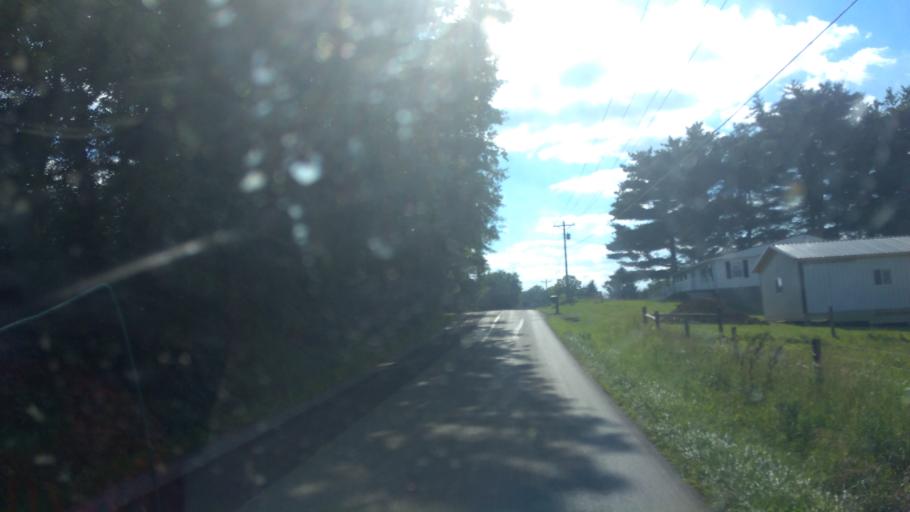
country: US
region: Ohio
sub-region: Wayne County
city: Apple Creek
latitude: 40.7262
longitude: -81.8891
